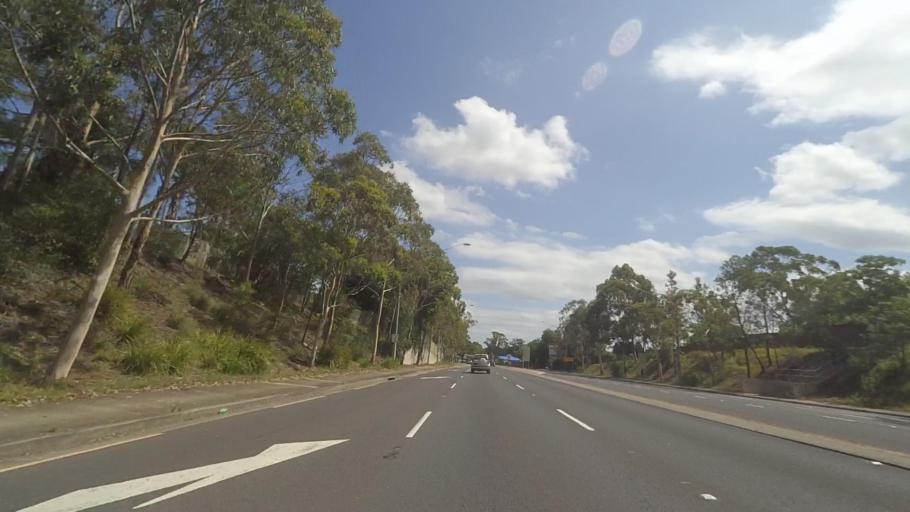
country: AU
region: New South Wales
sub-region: The Hills Shire
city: West Pennant
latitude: -33.7611
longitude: 151.0486
